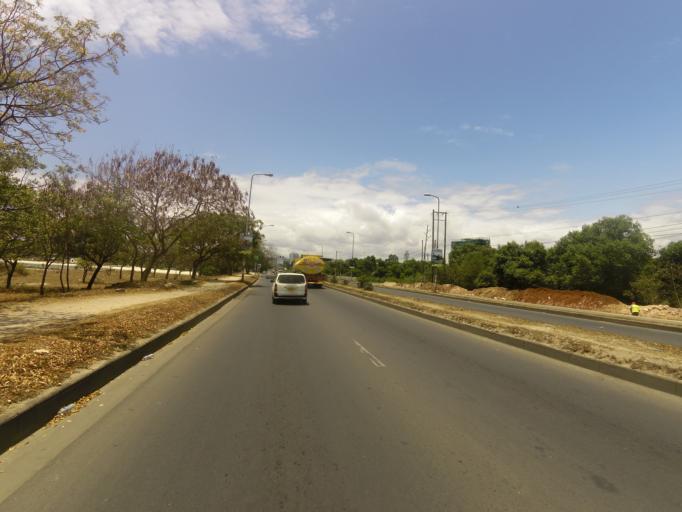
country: TZ
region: Dar es Salaam
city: Dar es Salaam
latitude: -6.7950
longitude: 39.2809
